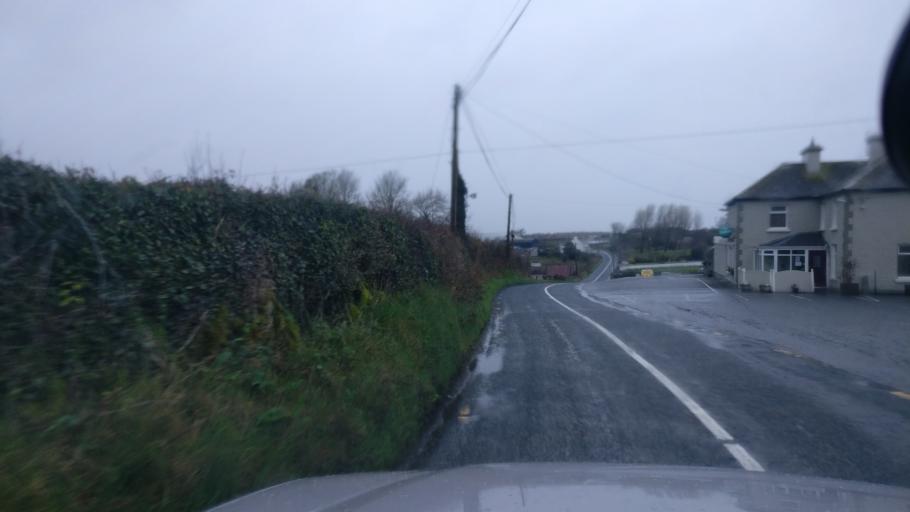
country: IE
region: Connaught
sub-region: County Galway
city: Loughrea
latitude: 53.1145
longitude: -8.4401
